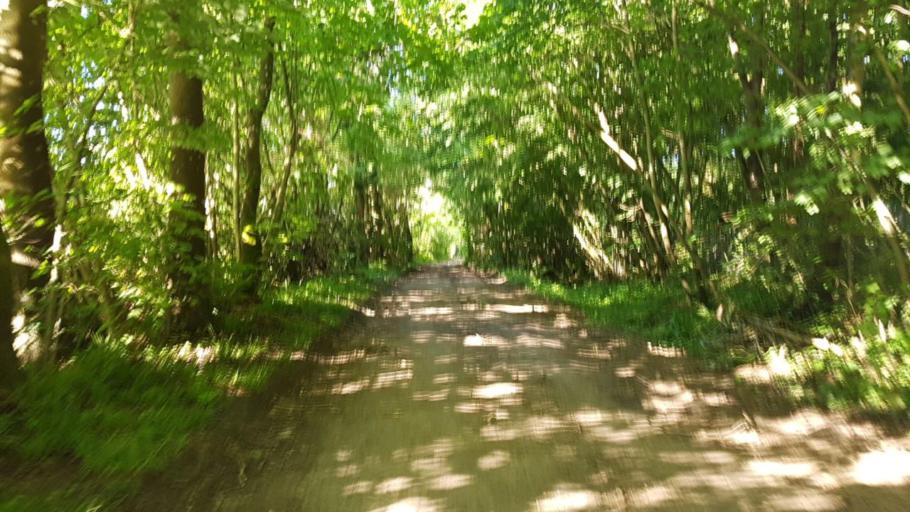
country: FR
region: Picardie
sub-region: Departement de l'Aisne
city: Essomes-sur-Marne
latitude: 49.0244
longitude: 3.3800
